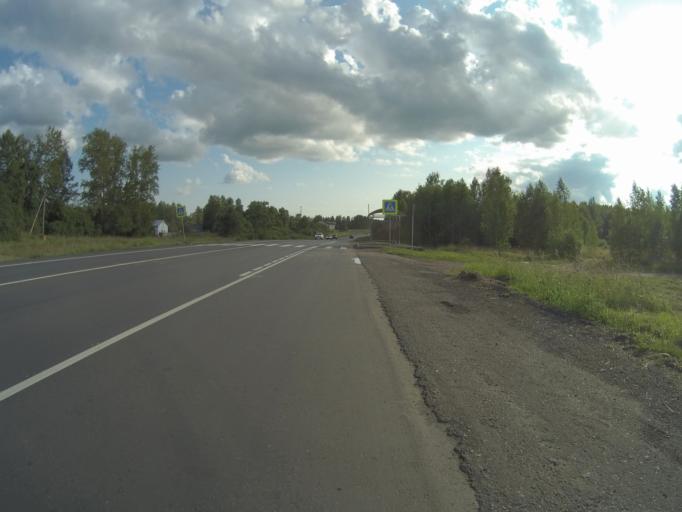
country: RU
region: Vladimir
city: Kideksha
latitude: 56.5026
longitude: 40.5402
